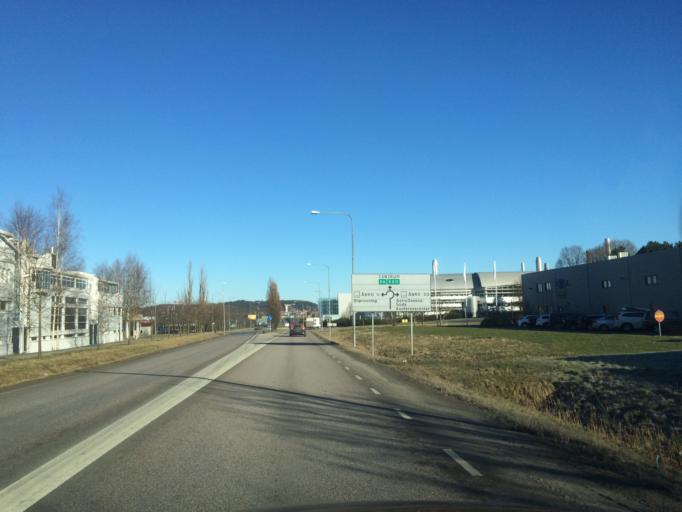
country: SE
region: Vaestra Goetaland
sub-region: Molndal
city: Moelndal
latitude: 57.6405
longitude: 12.0195
